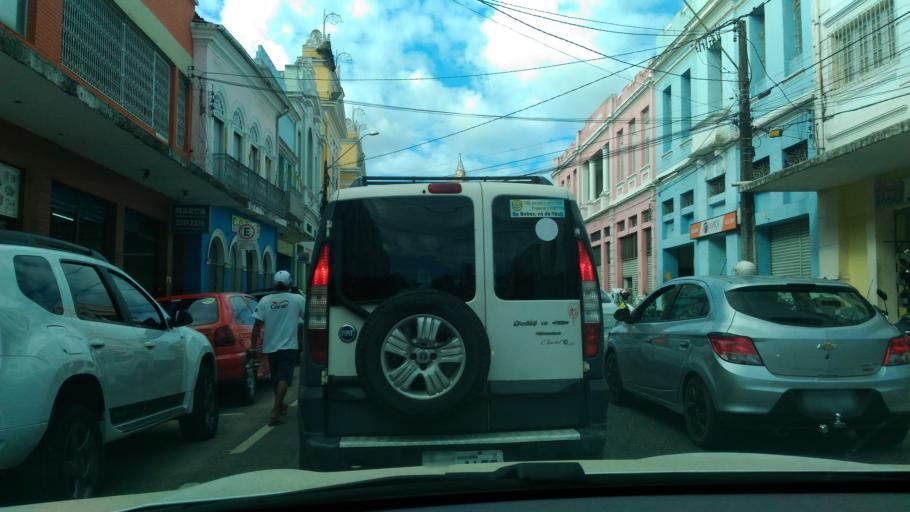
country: BR
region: Paraiba
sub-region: Joao Pessoa
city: Joao Pessoa
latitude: -7.1146
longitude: -34.8888
